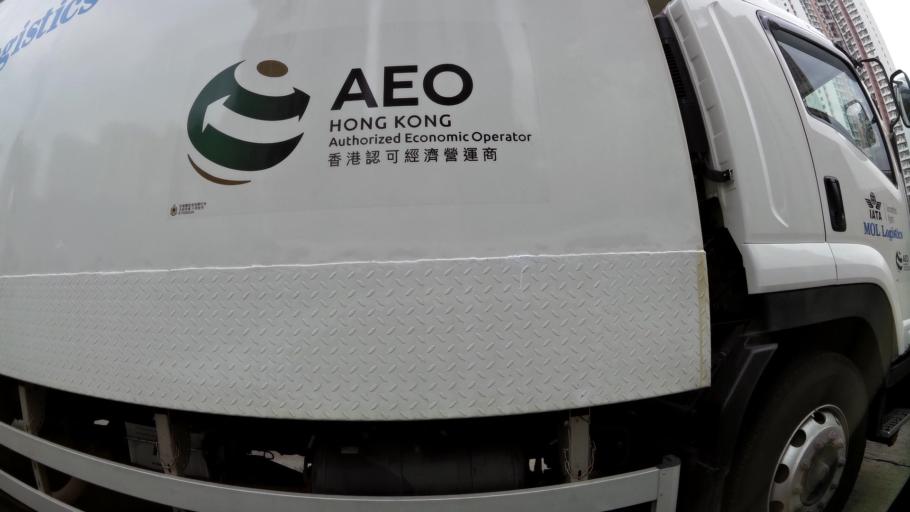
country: HK
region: Yuen Long
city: Yuen Long Kau Hui
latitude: 22.4596
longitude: 113.9975
